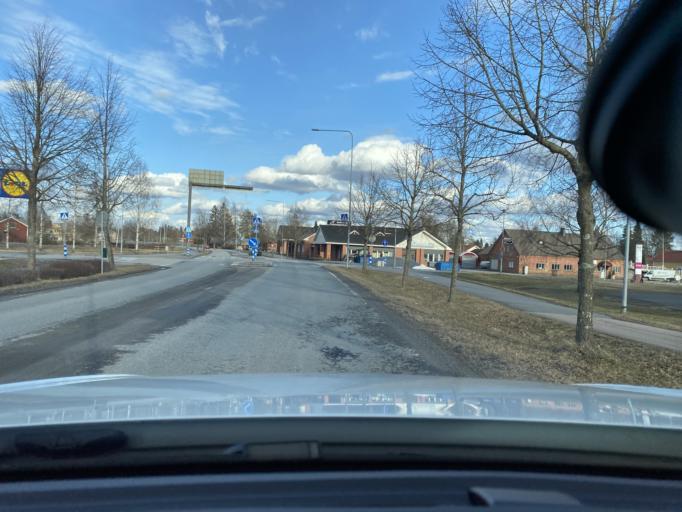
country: FI
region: Satakunta
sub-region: Pori
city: Huittinen
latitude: 61.1735
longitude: 22.6877
